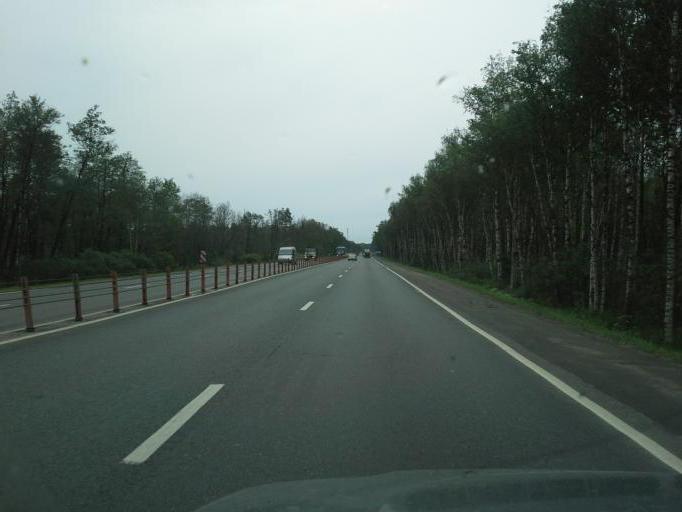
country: RU
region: Moskovskaya
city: Malaya Dubna
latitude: 55.8945
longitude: 39.0374
